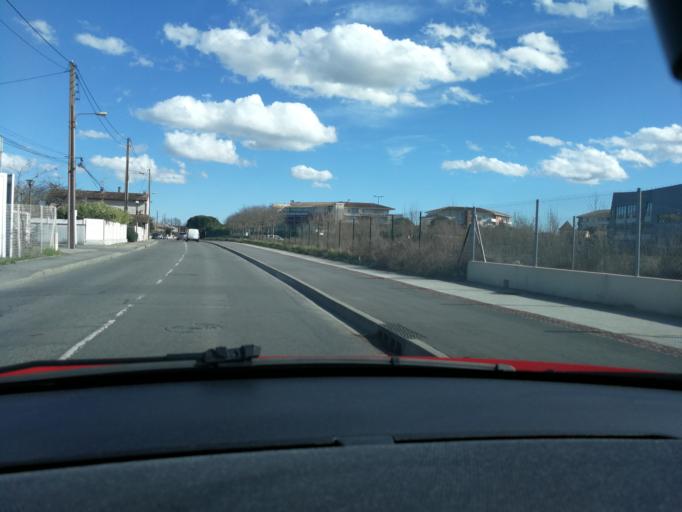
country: FR
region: Midi-Pyrenees
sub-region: Departement de la Haute-Garonne
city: Cugnaux
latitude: 43.5599
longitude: 1.3613
